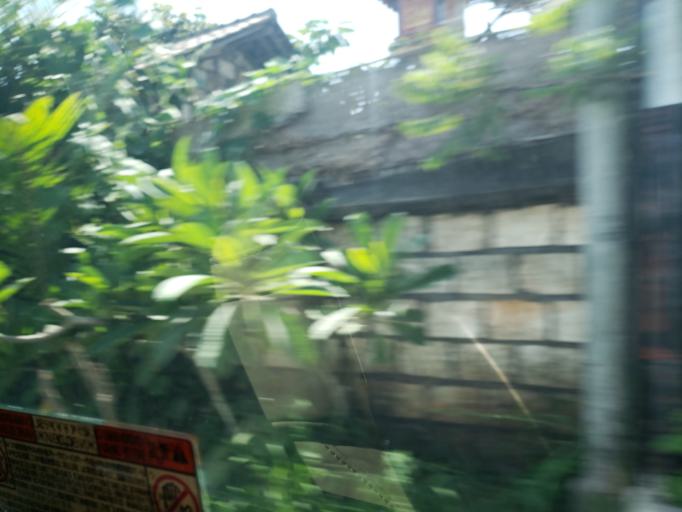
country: ID
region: Bali
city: Kangin
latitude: -8.8322
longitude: 115.1495
